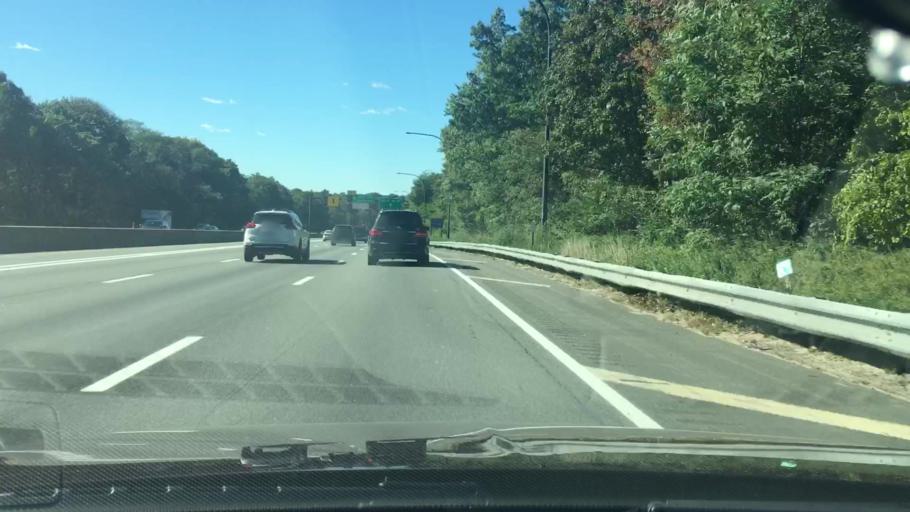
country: US
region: New York
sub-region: Nassau County
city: Old Westbury
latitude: 40.7821
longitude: -73.5975
